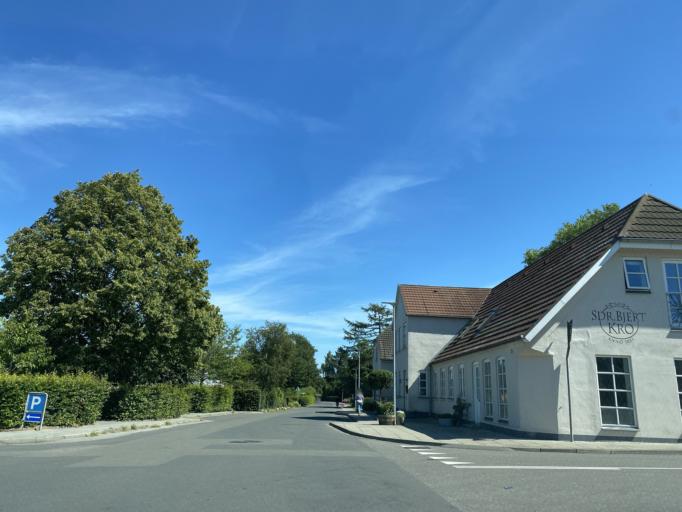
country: DK
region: South Denmark
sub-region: Kolding Kommune
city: Sonder Bjert
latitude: 55.4531
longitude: 9.5588
